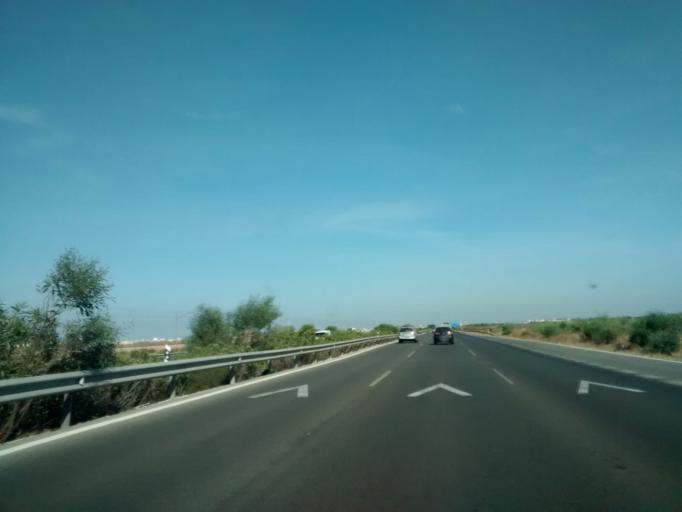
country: ES
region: Andalusia
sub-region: Provincia de Cadiz
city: Chiclana de la Frontera
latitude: 36.4557
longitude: -6.1554
